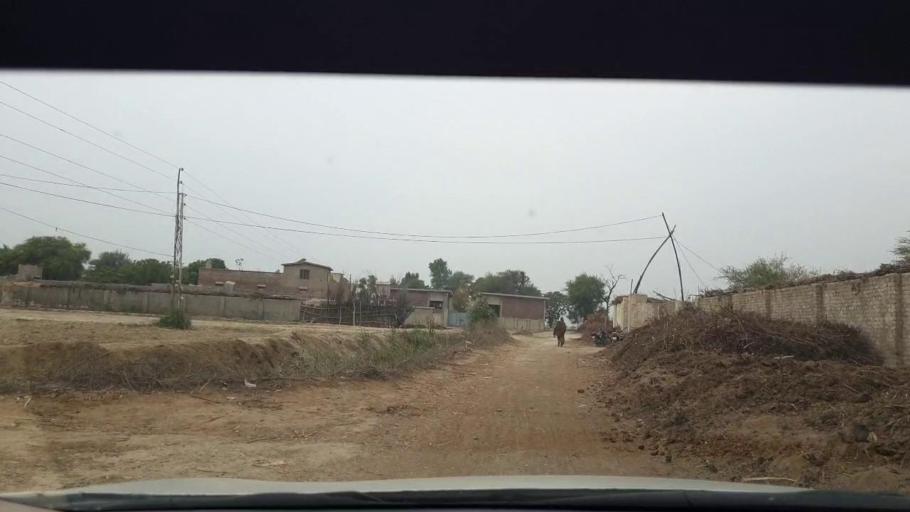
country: PK
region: Sindh
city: Berani
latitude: 25.8566
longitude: 68.7915
